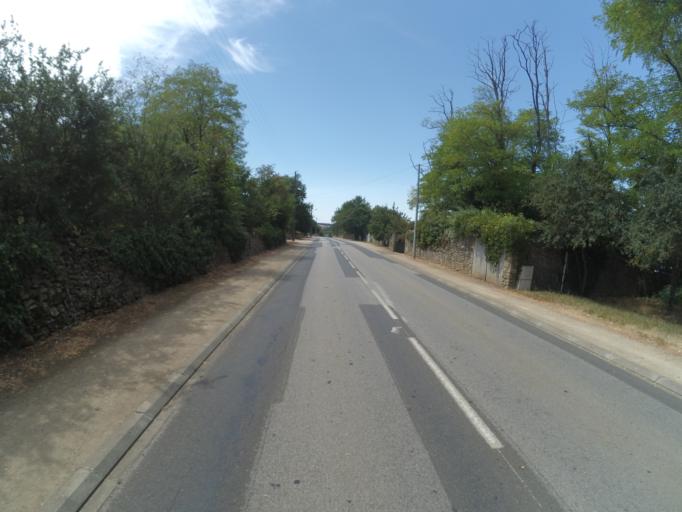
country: FR
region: Poitou-Charentes
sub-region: Departement de la Vienne
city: Vivonne
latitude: 46.4212
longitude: 0.2640
